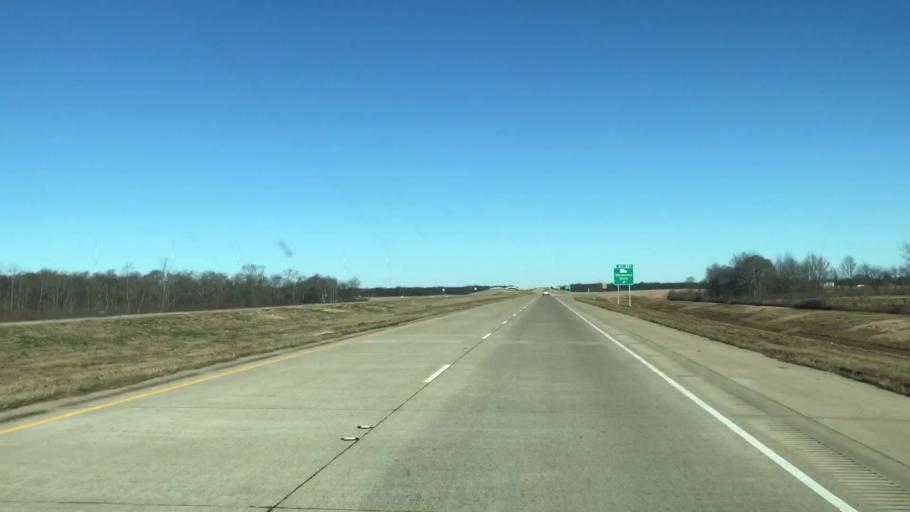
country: US
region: Louisiana
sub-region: Caddo Parish
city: Blanchard
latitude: 32.6680
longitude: -93.8472
